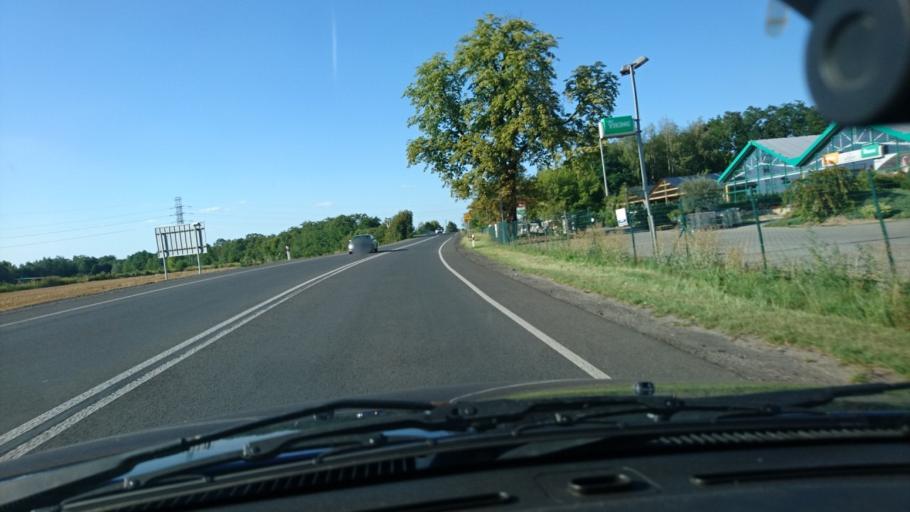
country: PL
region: Silesian Voivodeship
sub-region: Powiat gliwicki
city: Pyskowice
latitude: 50.3719
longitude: 18.6350
